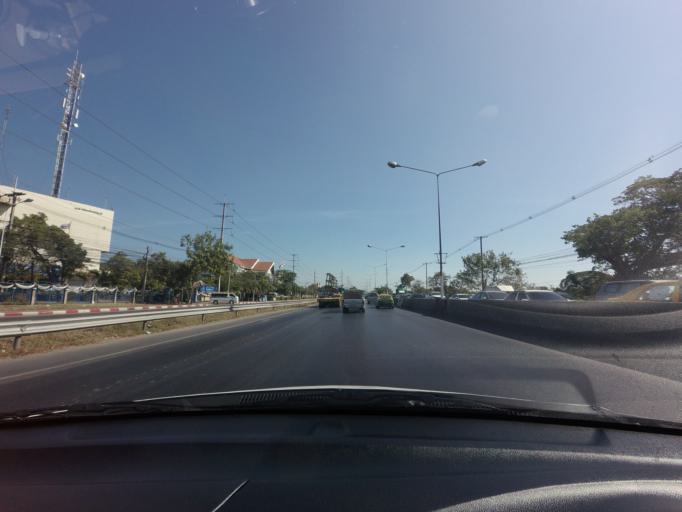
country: TH
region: Pathum Thani
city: Thanyaburi
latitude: 14.0185
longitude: 100.7303
